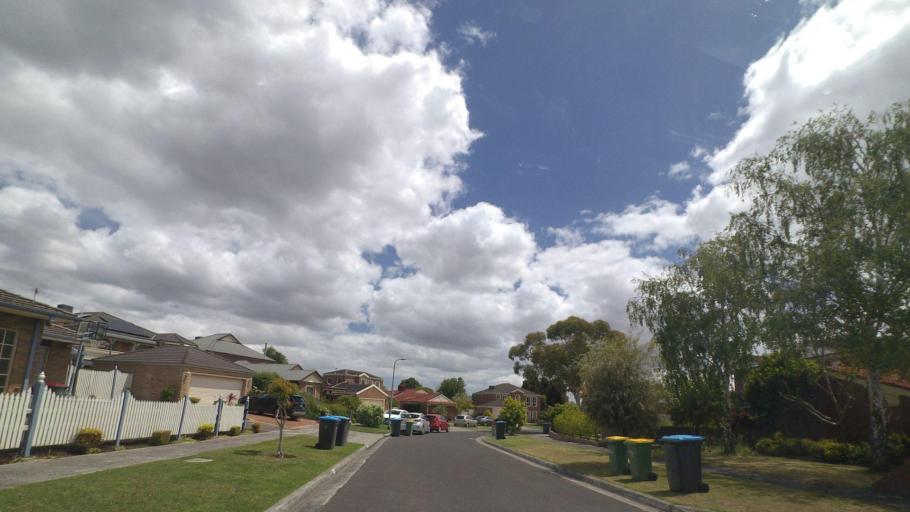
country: AU
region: Victoria
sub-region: Knox
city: Knoxfield
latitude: -37.8786
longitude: 145.2426
